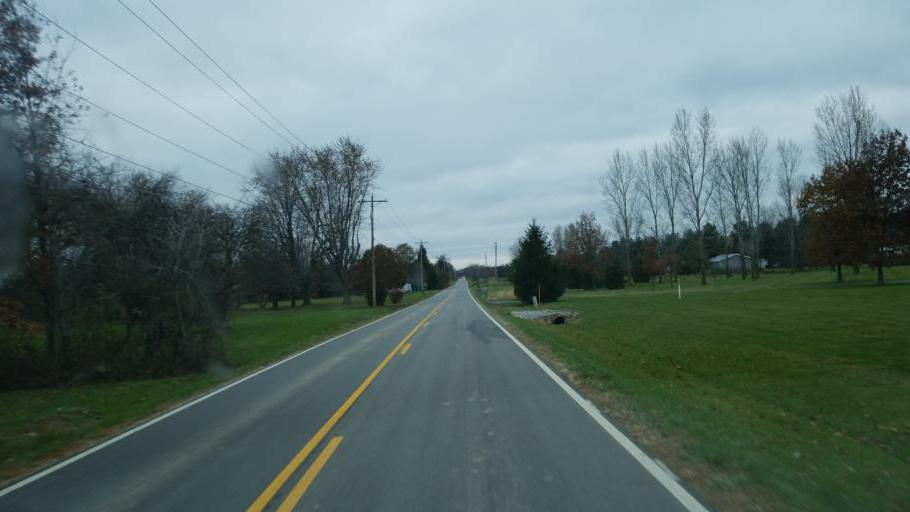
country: US
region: Ohio
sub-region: Franklin County
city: New Albany
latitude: 40.1578
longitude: -82.8396
